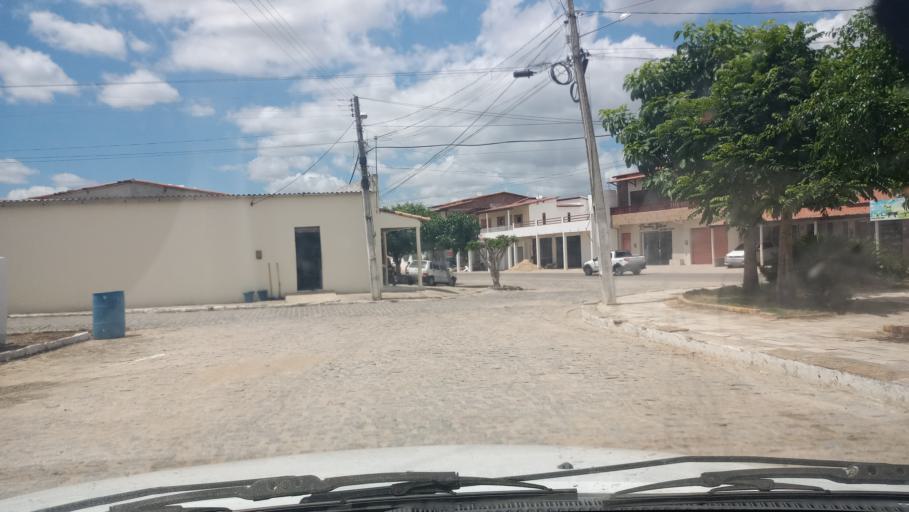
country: BR
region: Rio Grande do Norte
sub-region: Nova Cruz
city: Nova Cruz
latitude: -6.4594
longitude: -35.5795
